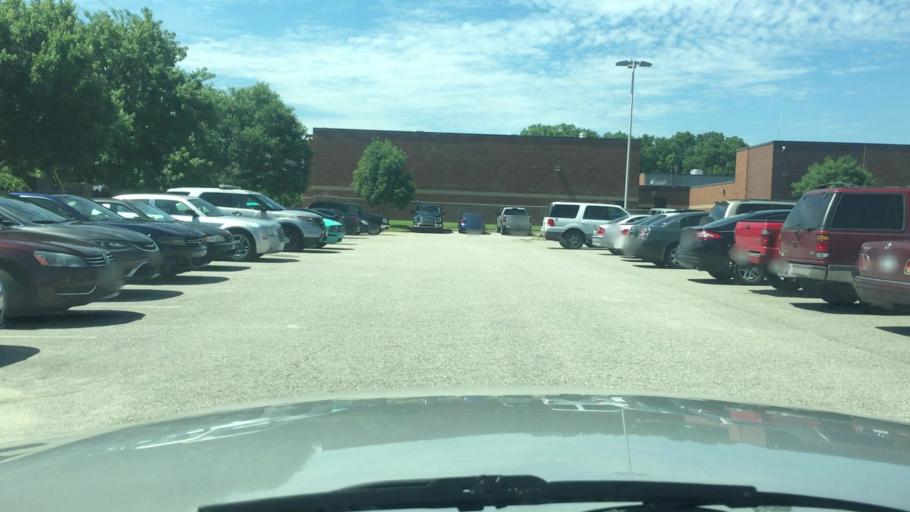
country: US
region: North Carolina
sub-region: Cumberland County
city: Fayetteville
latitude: 35.0495
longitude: -78.8796
